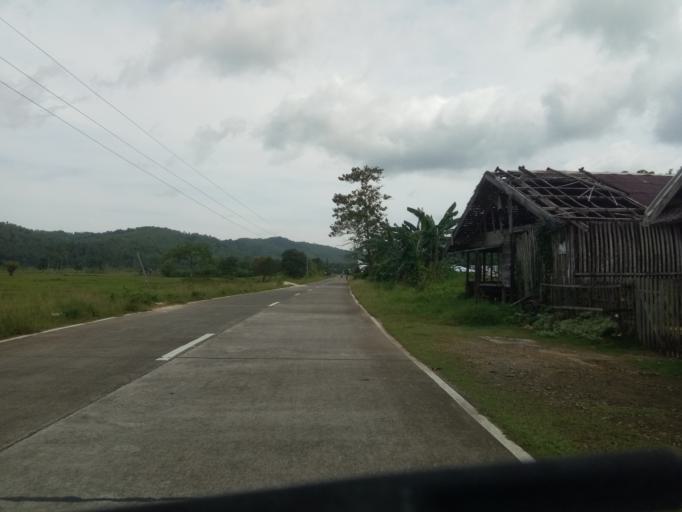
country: PH
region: Caraga
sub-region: Province of Surigao del Norte
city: Pilar
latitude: 9.8912
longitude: 126.0715
